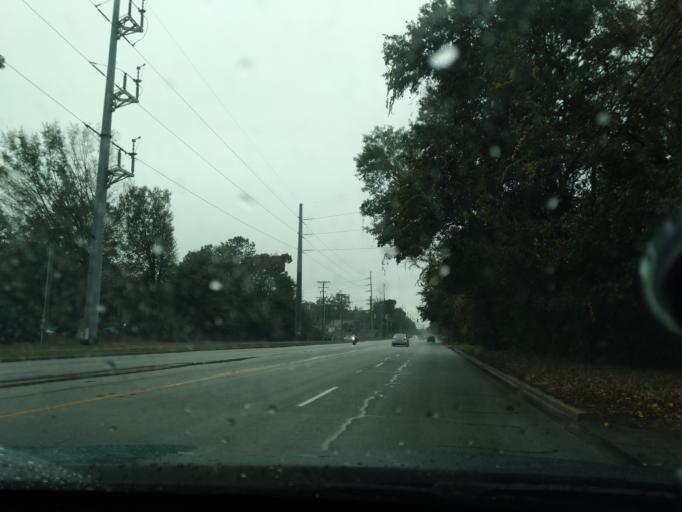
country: US
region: South Carolina
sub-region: Charleston County
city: Charleston
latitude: 32.7208
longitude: -79.9665
